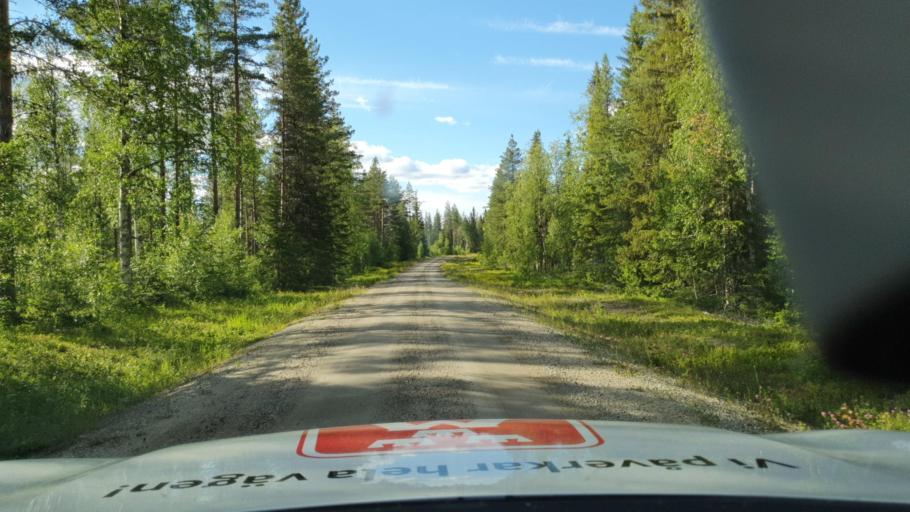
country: SE
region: Vaesterbotten
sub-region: Lycksele Kommun
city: Lycksele
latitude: 64.4634
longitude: 18.3006
